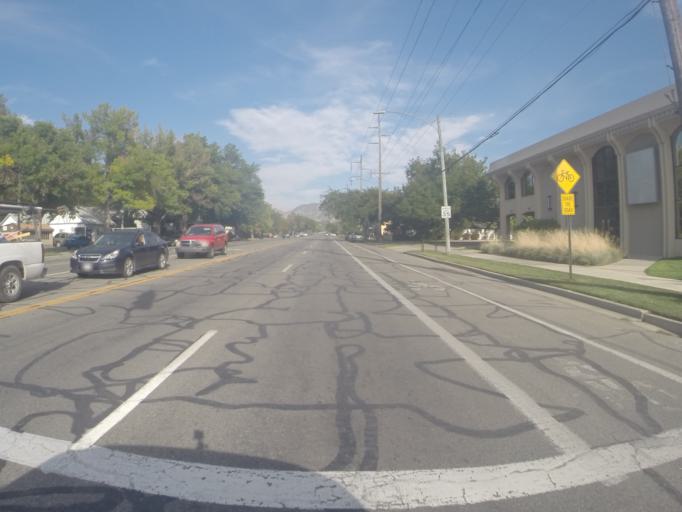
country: US
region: Utah
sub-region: Salt Lake County
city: Salt Lake City
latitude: 40.7519
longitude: -111.8852
